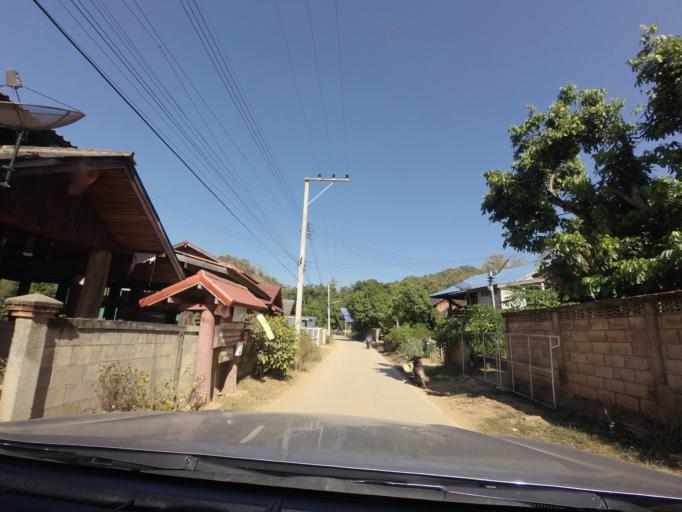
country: TH
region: Lampang
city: Chae Hom
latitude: 18.6039
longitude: 99.6306
